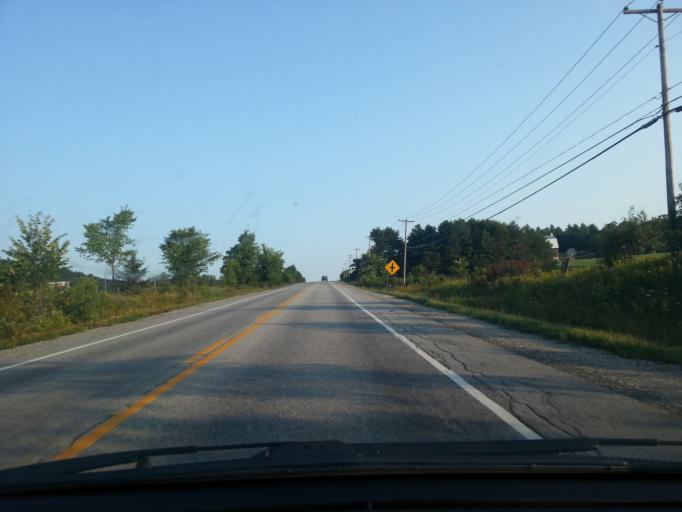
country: CA
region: Quebec
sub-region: Outaouais
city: Wakefield
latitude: 45.6033
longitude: -75.9042
